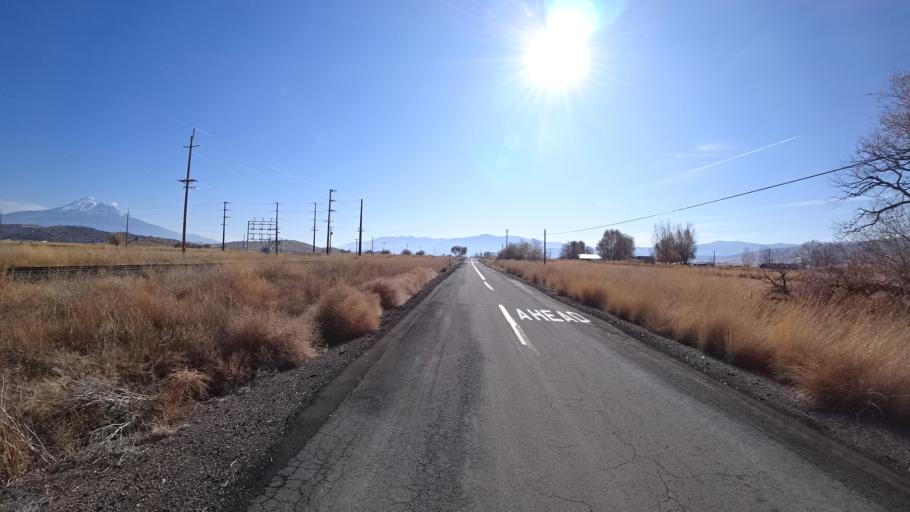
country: US
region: California
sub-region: Siskiyou County
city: Montague
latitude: 41.6049
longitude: -122.5233
